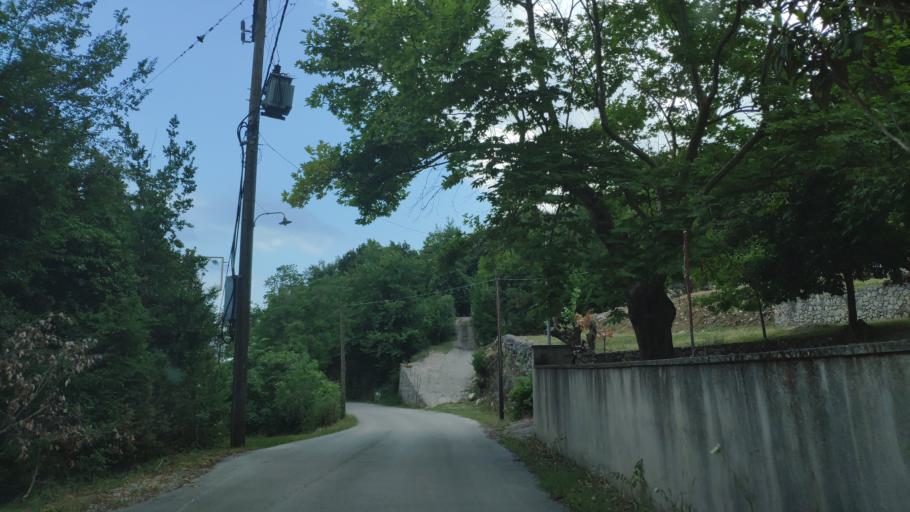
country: GR
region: Epirus
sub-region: Nomos Artas
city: Agios Dimitrios
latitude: 39.4342
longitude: 21.0157
